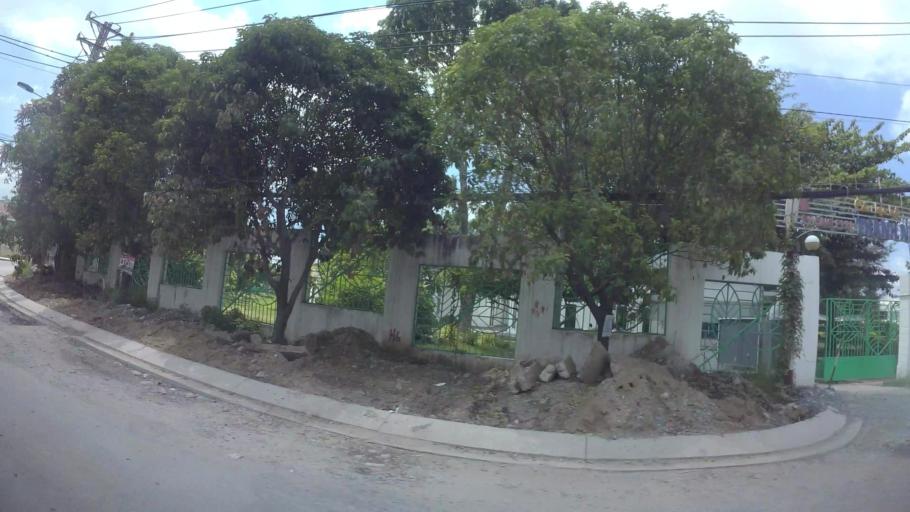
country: VN
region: Ho Chi Minh City
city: Quan Chin
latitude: 10.8326
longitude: 106.7775
